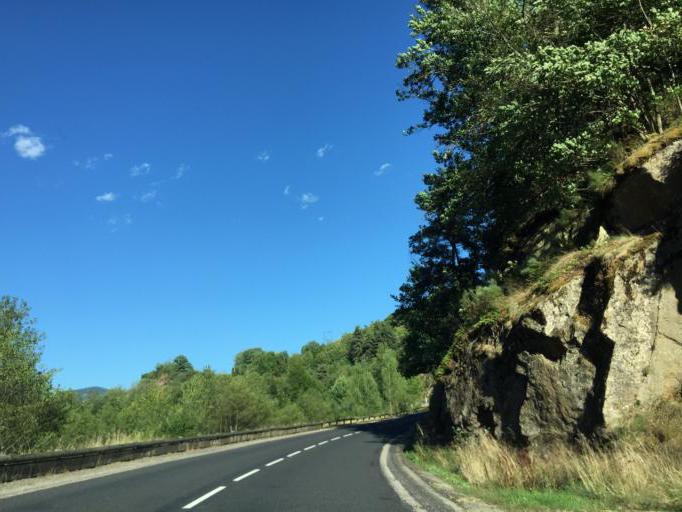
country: FR
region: Auvergne
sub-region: Departement de la Haute-Loire
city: Saugues
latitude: 44.9654
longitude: 3.6329
